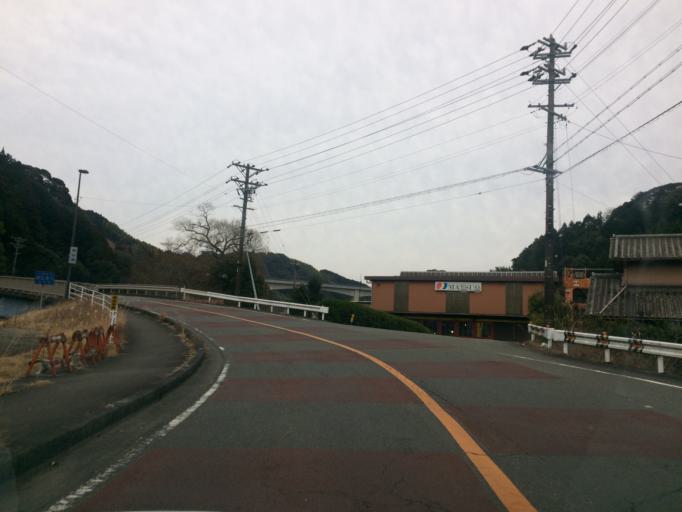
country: JP
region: Shizuoka
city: Fujieda
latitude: 34.9308
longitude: 138.2683
